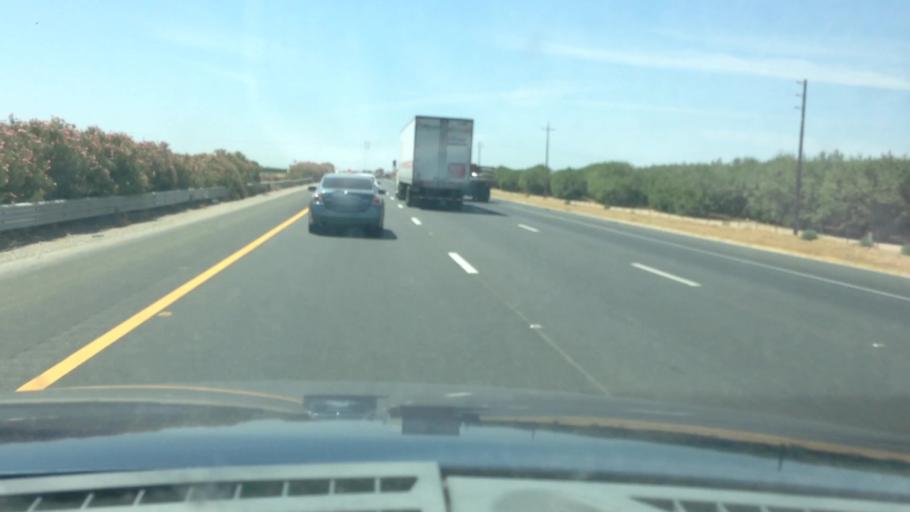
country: US
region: California
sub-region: Kern County
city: McFarland
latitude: 35.6262
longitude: -119.2152
